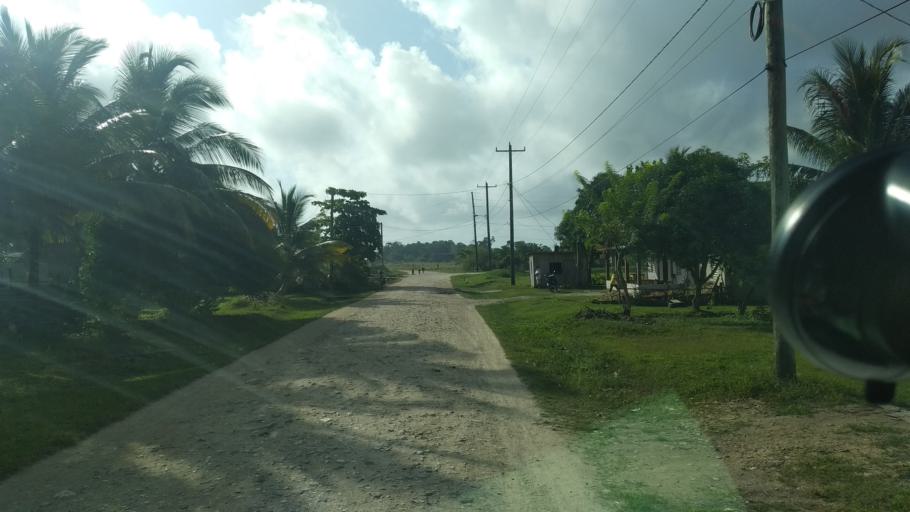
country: BZ
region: Stann Creek
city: Placencia
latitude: 16.5094
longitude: -88.5452
